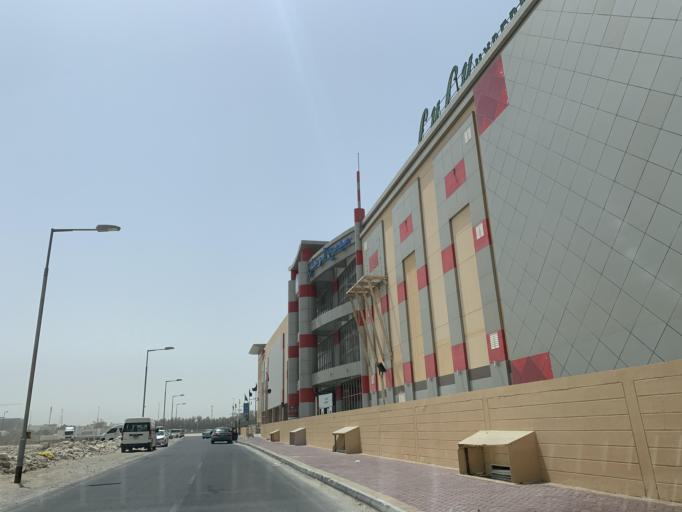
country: BH
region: Northern
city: Madinat `Isa
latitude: 26.1632
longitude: 50.5237
